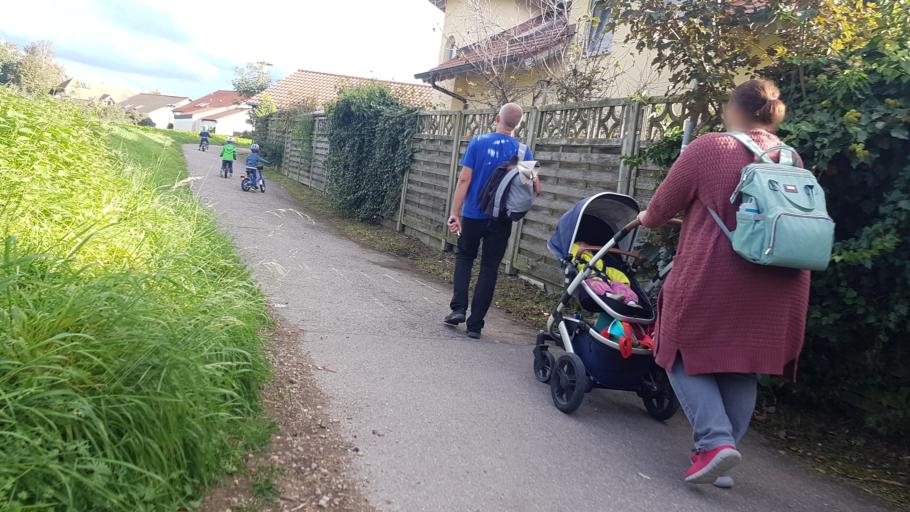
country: DE
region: Baden-Wuerttemberg
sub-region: Tuebingen Region
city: Immenstaad am Bodensee
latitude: 47.6644
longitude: 9.3518
